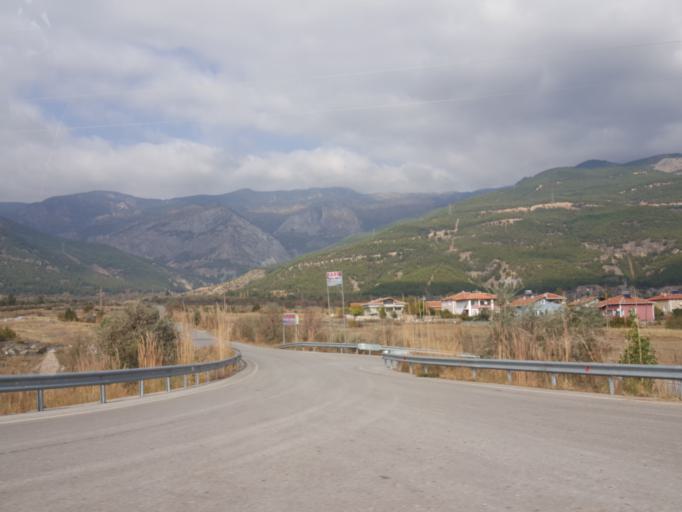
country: TR
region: Corum
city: Hacihamza
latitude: 41.1294
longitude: 34.4241
